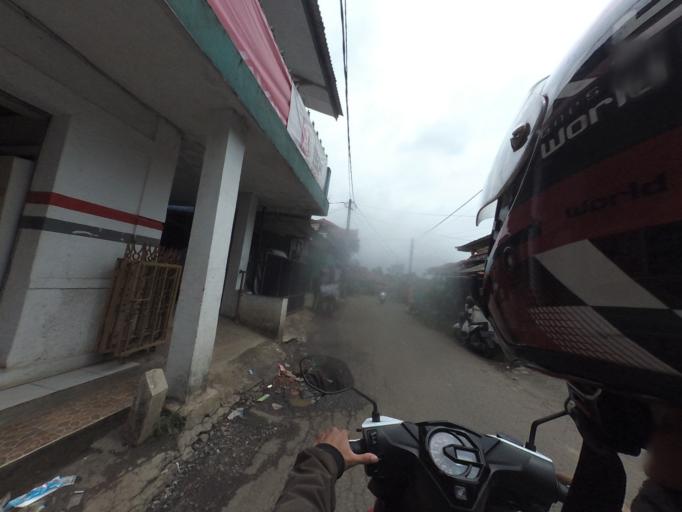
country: ID
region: West Java
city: Bogor
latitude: -6.6092
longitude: 106.7564
